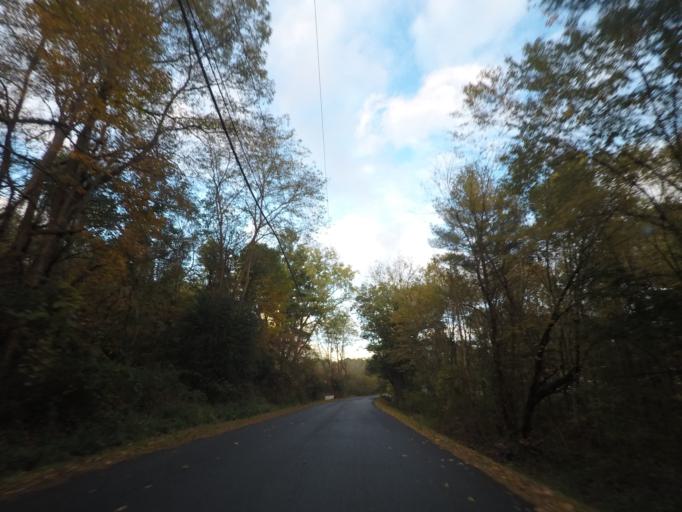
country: US
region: New York
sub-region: Rensselaer County
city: Nassau
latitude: 42.5520
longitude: -73.5926
